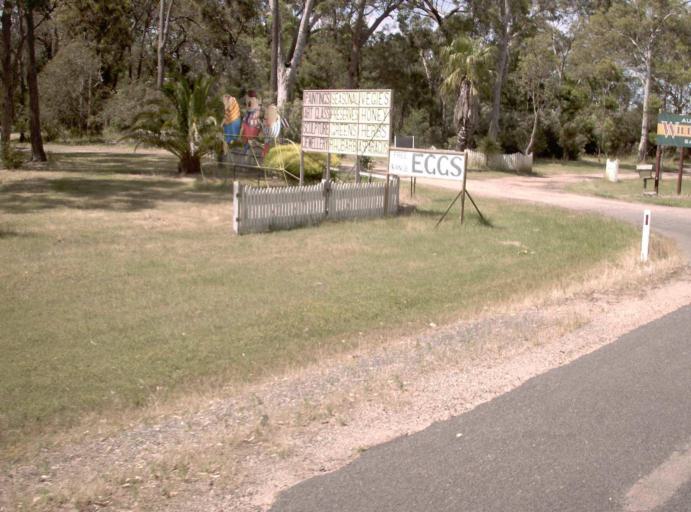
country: AU
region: Victoria
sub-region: Wellington
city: Sale
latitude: -37.9216
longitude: 147.2490
